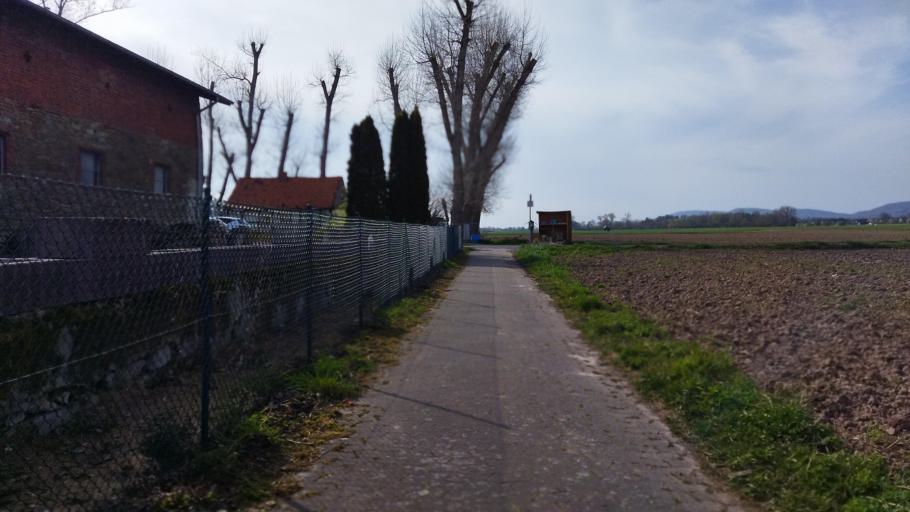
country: DE
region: Lower Saxony
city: Hessisch Oldendorf
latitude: 52.1635
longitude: 9.2122
